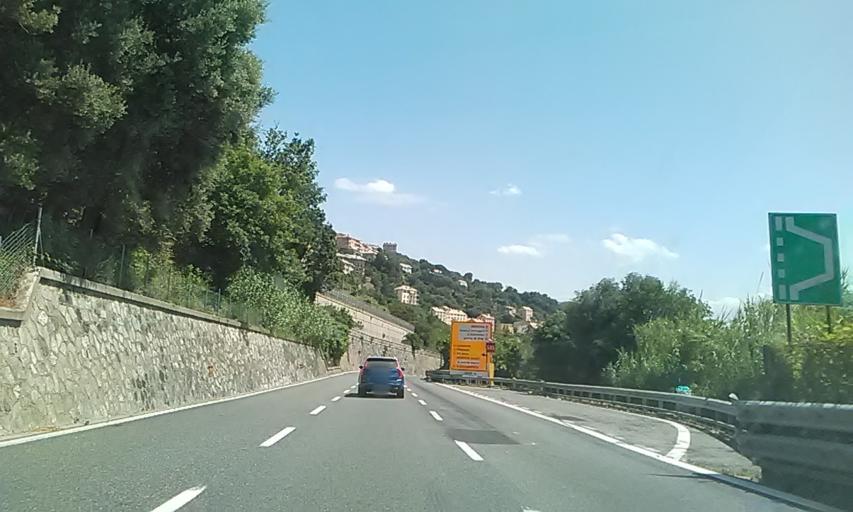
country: IT
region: Liguria
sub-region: Provincia di Genova
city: Mele
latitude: 44.4202
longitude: 8.7268
